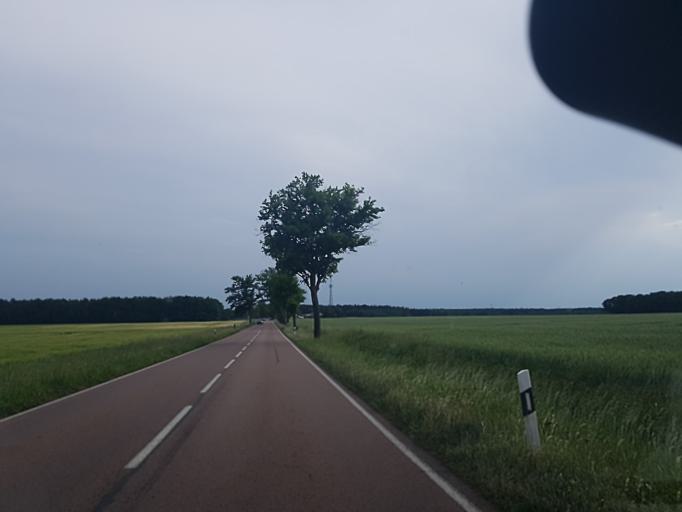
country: DE
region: Saxony-Anhalt
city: Nudersdorf
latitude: 51.9179
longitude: 12.6059
